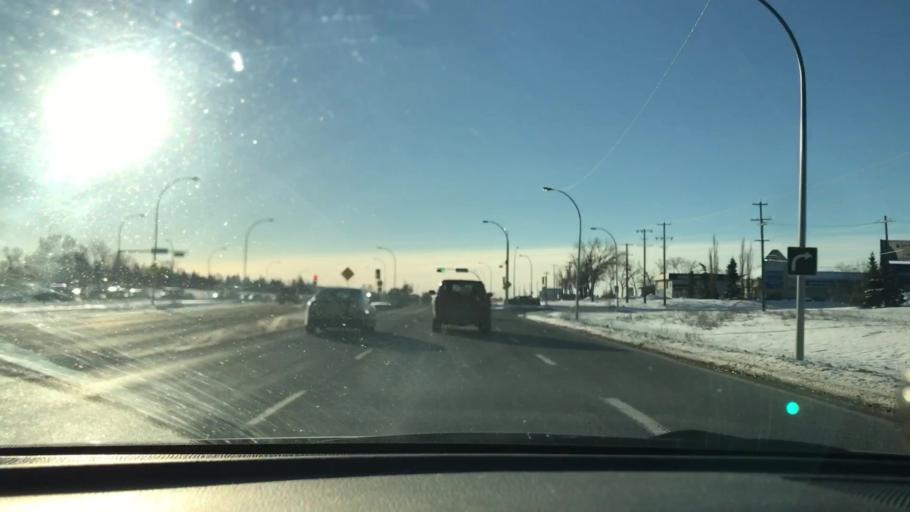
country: CA
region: Alberta
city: Edmonton
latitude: 53.4753
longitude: -113.4670
